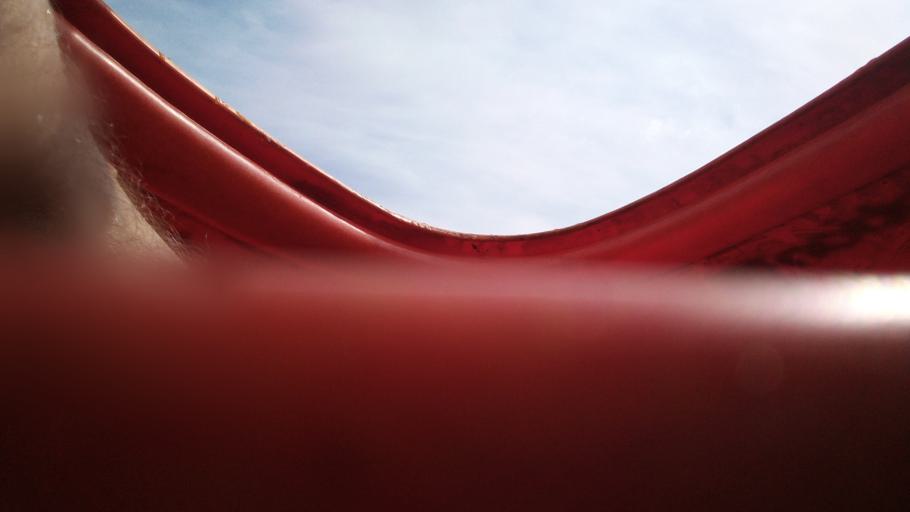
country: RU
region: Chelyabinsk
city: Turgoyak
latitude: 55.1777
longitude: 60.0337
